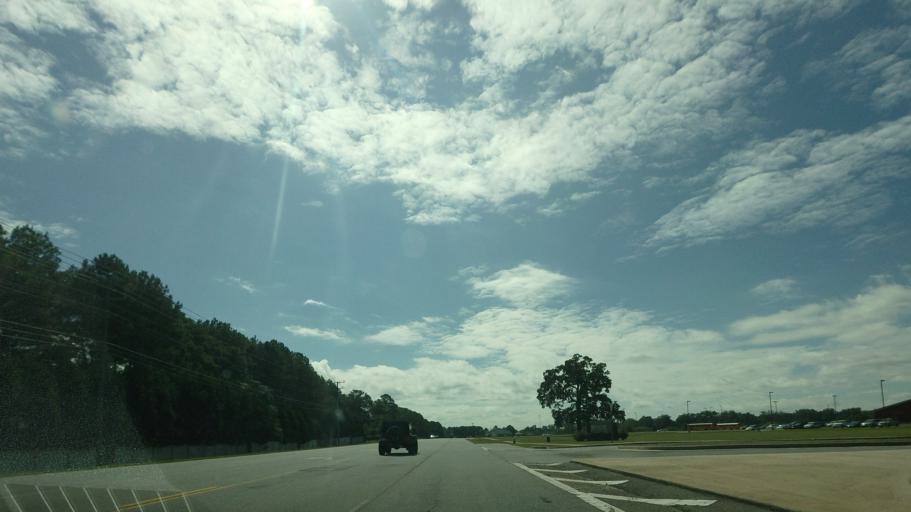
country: US
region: Georgia
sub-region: Houston County
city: Centerville
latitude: 32.5766
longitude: -83.6936
